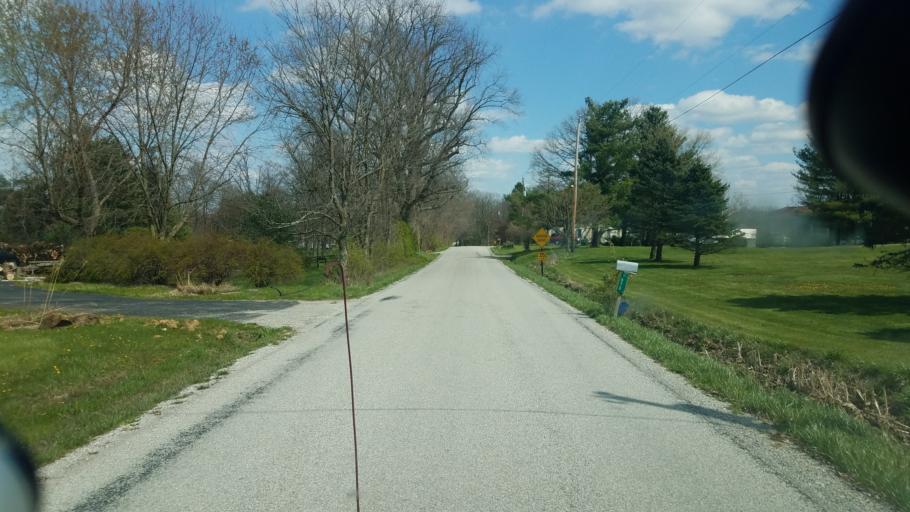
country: US
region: Ohio
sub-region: Licking County
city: Beechwood Trails
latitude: 40.0951
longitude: -82.6425
